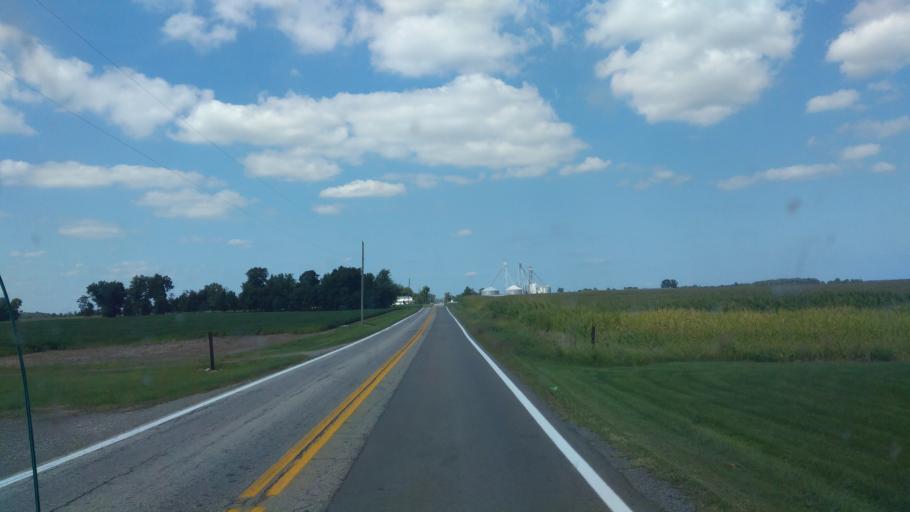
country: US
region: Ohio
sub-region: Union County
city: Marysville
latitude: 40.3743
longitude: -83.4542
